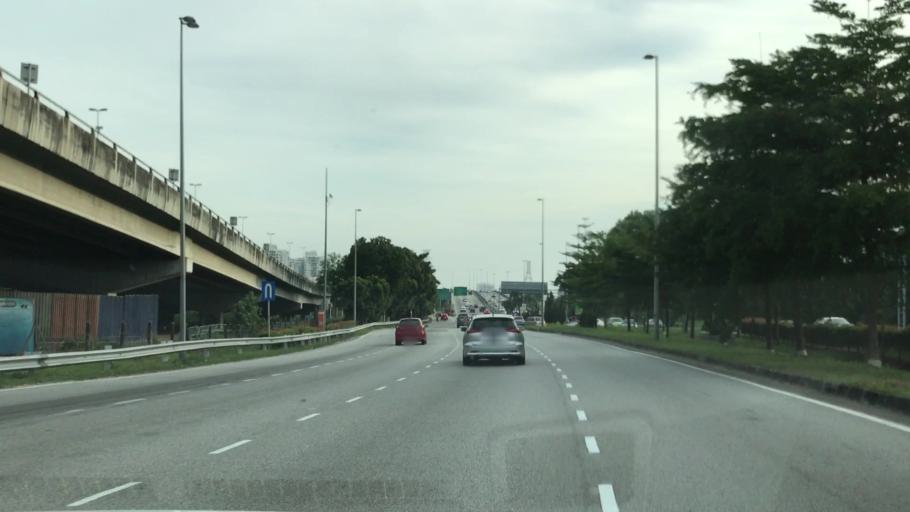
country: MY
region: Kuala Lumpur
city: Kuala Lumpur
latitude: 3.1042
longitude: 101.7056
